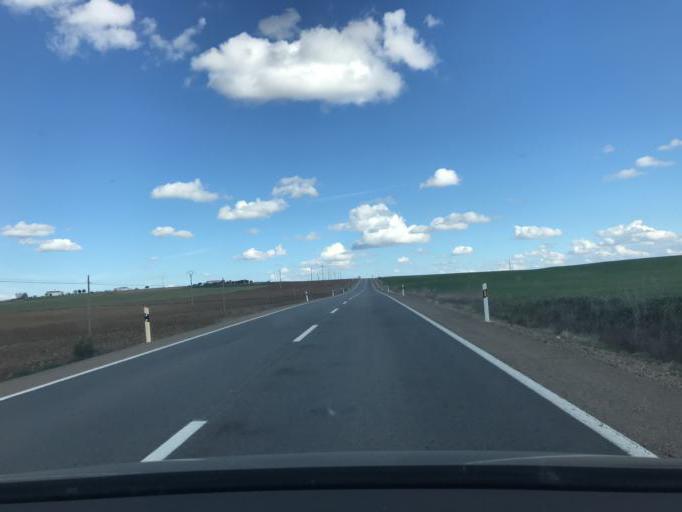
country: ES
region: Extremadura
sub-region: Provincia de Badajoz
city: Azuaga
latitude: 38.2962
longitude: -5.6458
